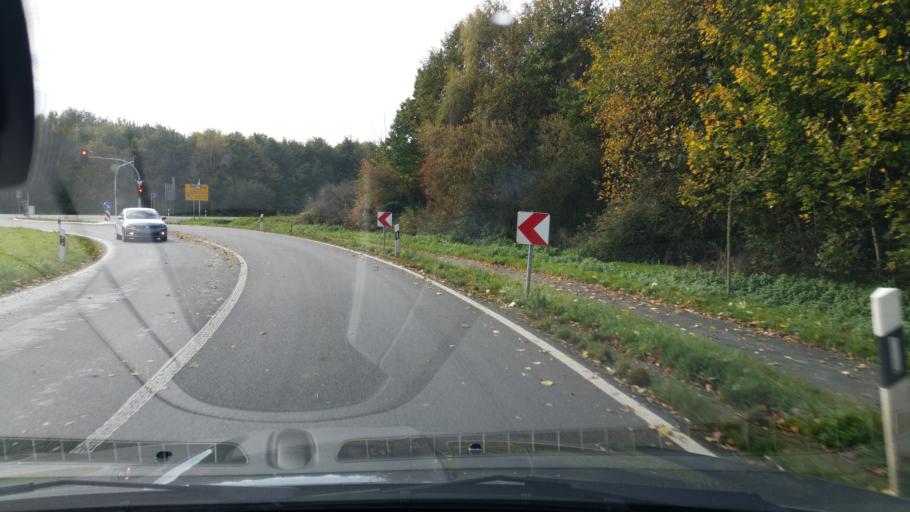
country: DE
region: North Rhine-Westphalia
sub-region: Regierungsbezirk Munster
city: Isselburg
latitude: 51.8135
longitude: 6.5140
